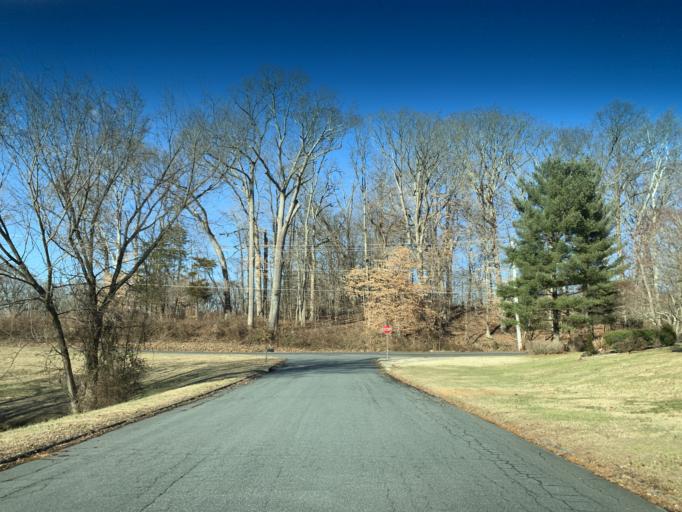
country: US
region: Maryland
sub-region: Harford County
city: Riverside
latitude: 39.5345
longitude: -76.2543
